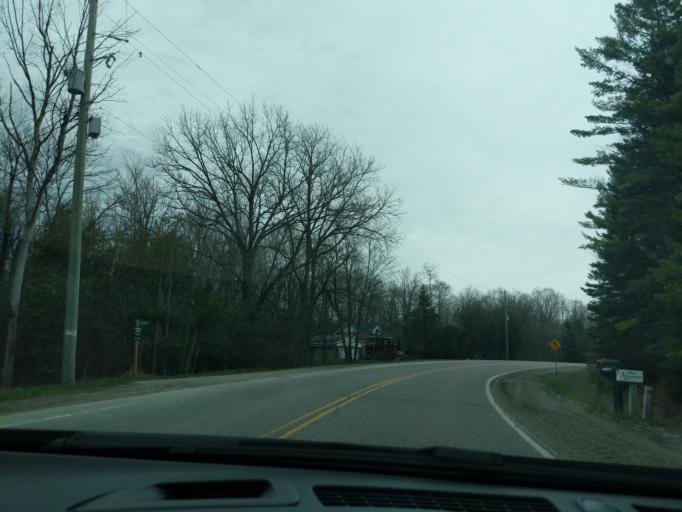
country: CA
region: Ontario
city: Orangeville
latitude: 44.0015
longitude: -80.0011
